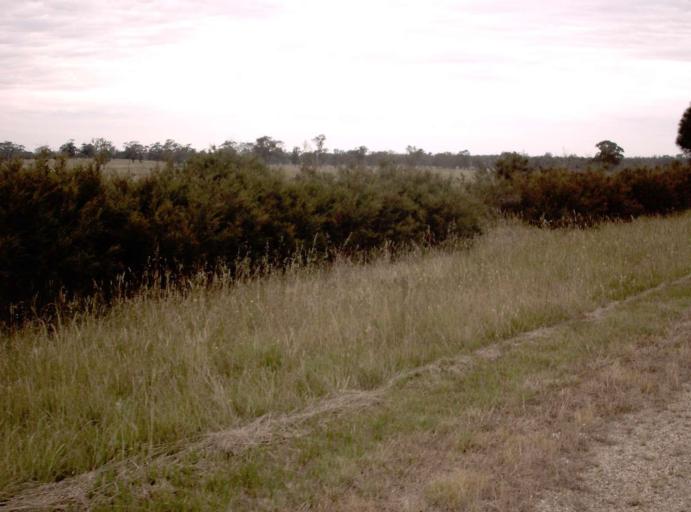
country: AU
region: Victoria
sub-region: Wellington
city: Sale
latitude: -38.1728
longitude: 147.1141
